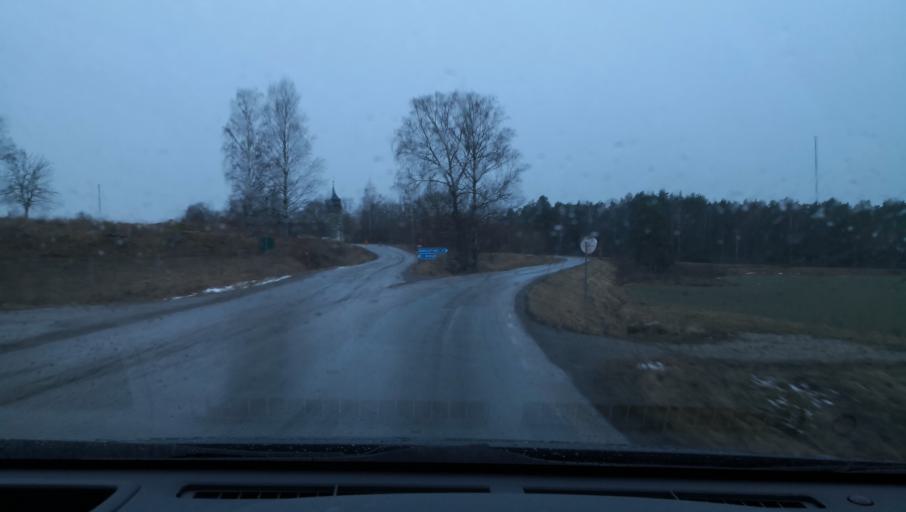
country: SE
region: Soedermanland
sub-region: Eskilstuna Kommun
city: Arla
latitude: 59.3991
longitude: 16.6781
